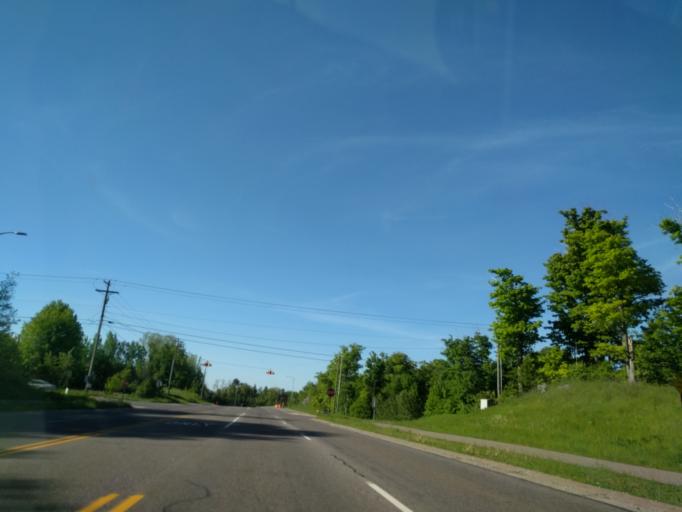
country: US
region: Michigan
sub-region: Marquette County
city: Marquette
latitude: 46.5358
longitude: -87.4171
